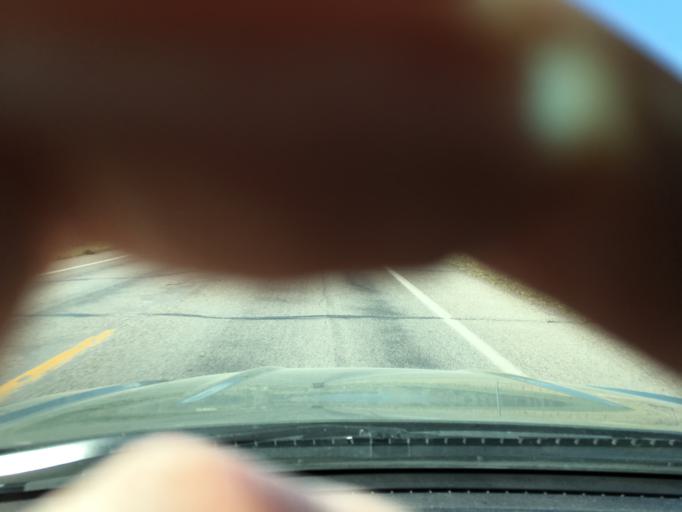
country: US
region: Colorado
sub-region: Delta County
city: Delta
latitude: 38.7654
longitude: -108.0040
